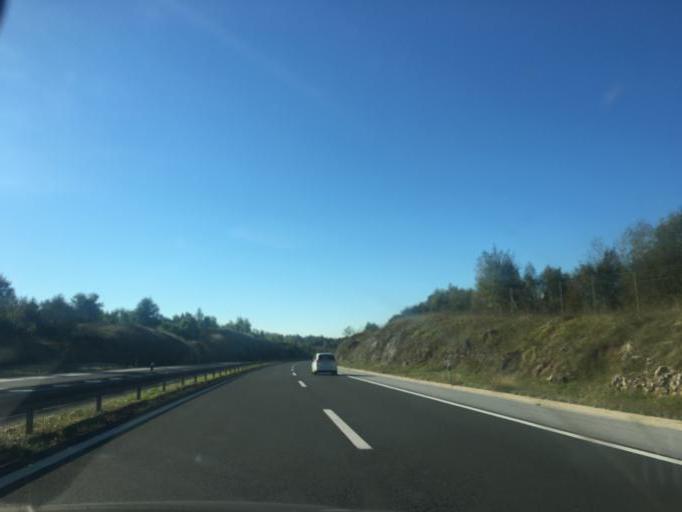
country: HR
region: Karlovacka
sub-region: Grad Ogulin
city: Ogulin
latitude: 45.3549
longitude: 15.2775
